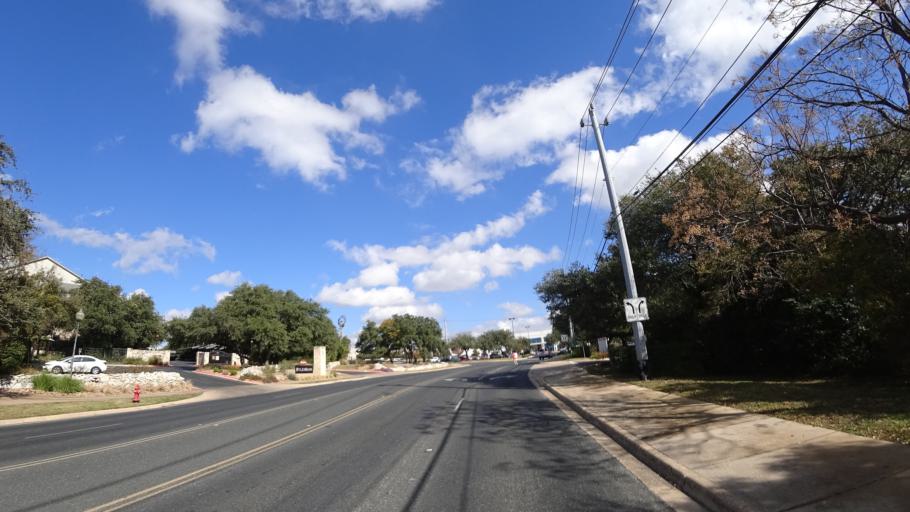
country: US
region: Texas
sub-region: Williamson County
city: Jollyville
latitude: 30.4315
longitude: -97.7393
